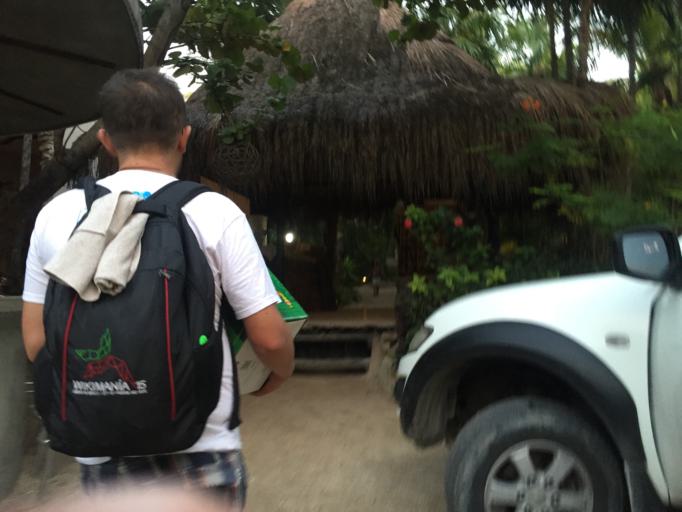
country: MX
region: Quintana Roo
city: Tulum
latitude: 20.1639
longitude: -87.4537
